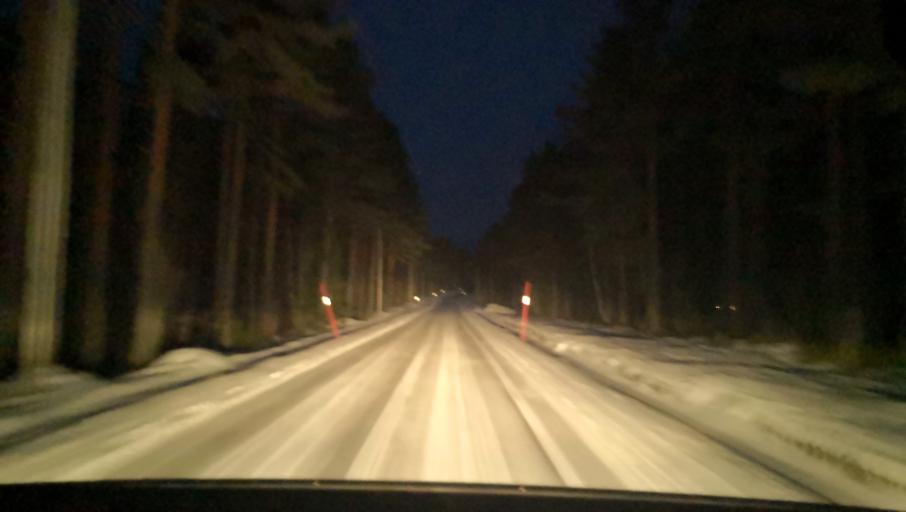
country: SE
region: Uppsala
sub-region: Heby Kommun
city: Tarnsjo
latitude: 60.2902
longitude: 16.8057
